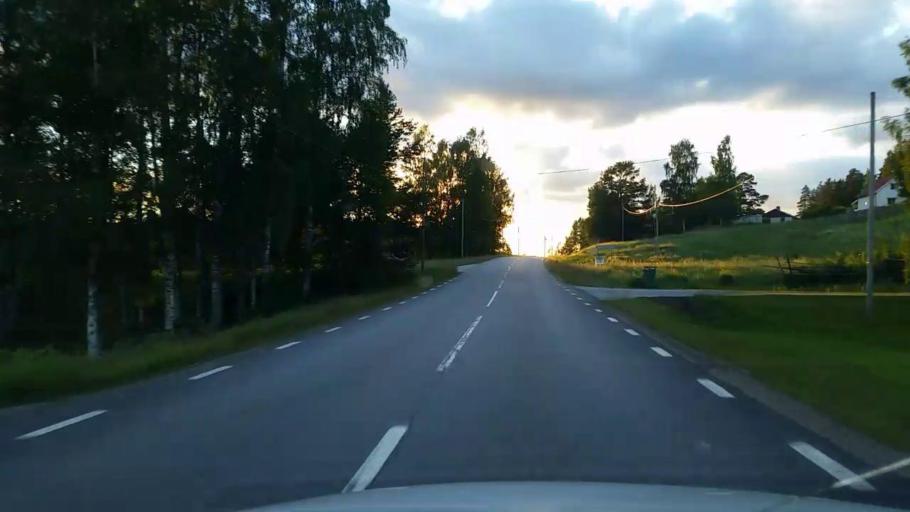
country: SE
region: Vaesternorrland
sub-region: Ange Kommun
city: Ange
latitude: 62.1531
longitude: 15.6799
